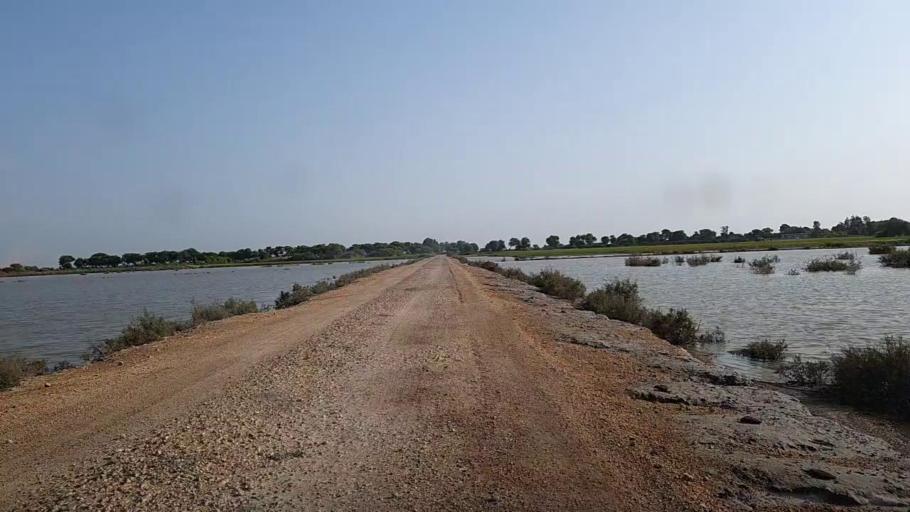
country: PK
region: Sindh
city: Bulri
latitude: 24.7737
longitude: 68.4355
